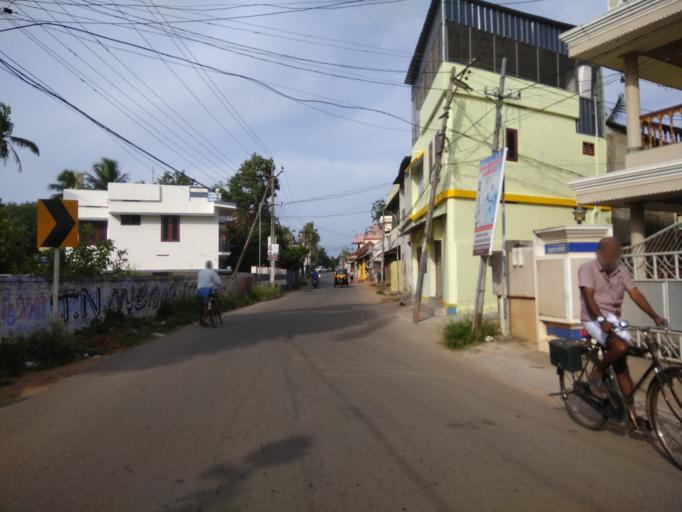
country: IN
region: Kerala
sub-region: Thiruvananthapuram
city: Thiruvananthapuram
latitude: 8.4520
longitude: 76.9983
